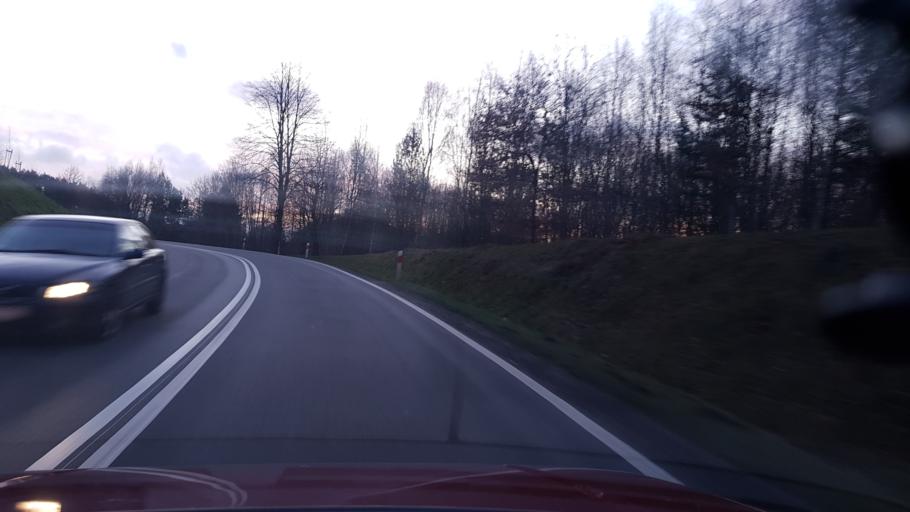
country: PL
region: Pomeranian Voivodeship
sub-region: Powiat bytowski
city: Bytow
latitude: 54.1403
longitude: 17.4369
